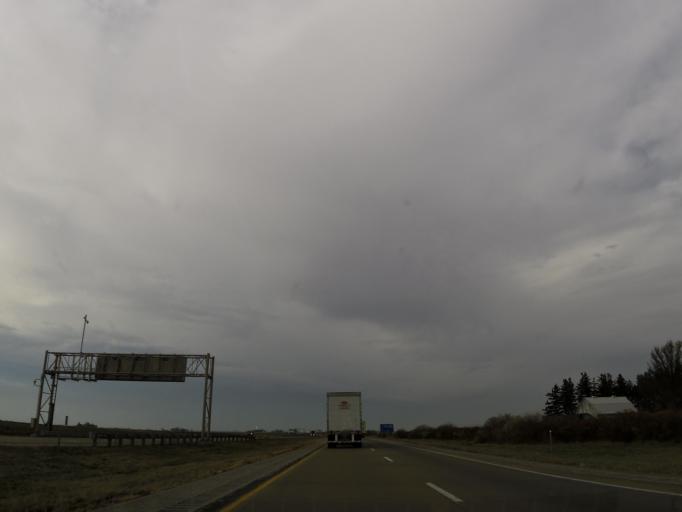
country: US
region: Iowa
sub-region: Scott County
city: Walcott
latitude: 41.6043
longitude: -90.7240
